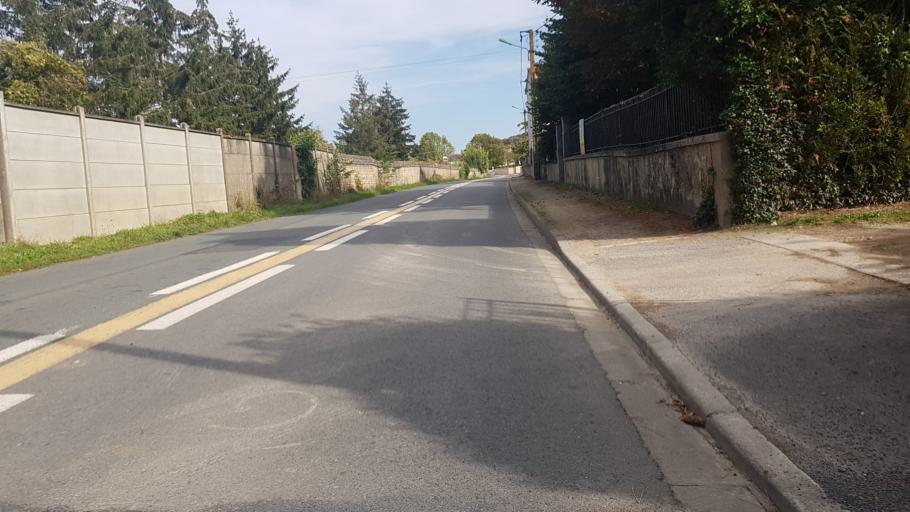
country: FR
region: Poitou-Charentes
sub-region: Departement de la Vienne
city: Chasseneuil-du-Poitou
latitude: 46.6284
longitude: 0.3669
